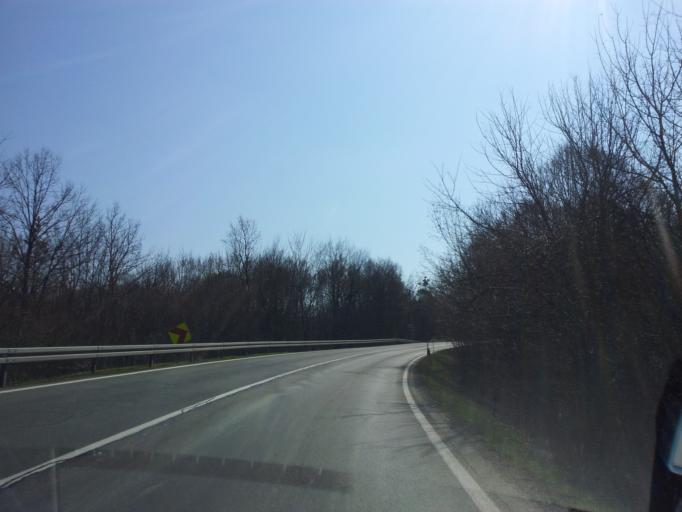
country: HR
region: Karlovacka
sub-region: Grad Karlovac
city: Slunj
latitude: 45.0476
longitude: 15.6304
